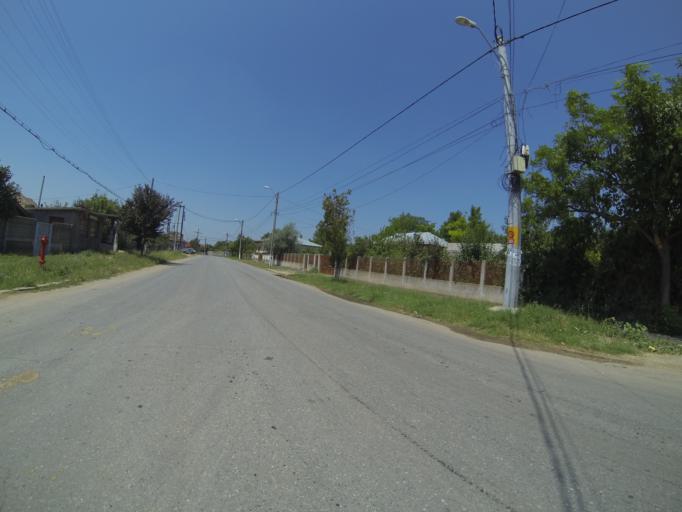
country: RO
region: Dolj
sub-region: Comuna Segarcea
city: Segarcea
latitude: 44.0936
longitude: 23.7527
